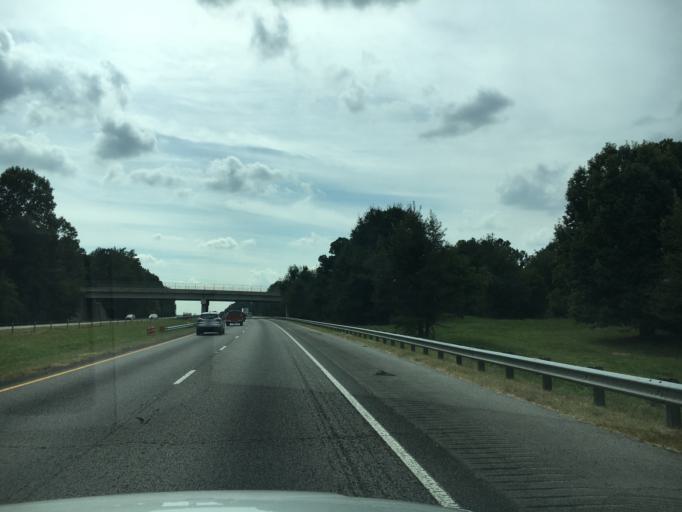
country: US
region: Georgia
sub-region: Jackson County
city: Hoschton
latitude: 34.0976
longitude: -83.8099
